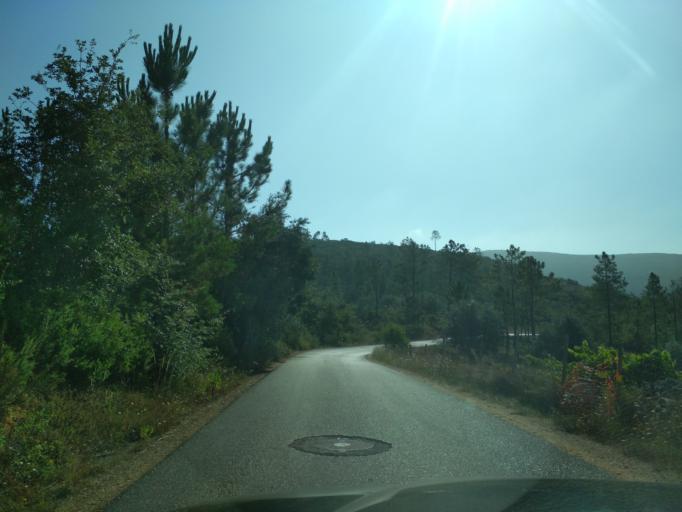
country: PT
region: Coimbra
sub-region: Soure
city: Soure
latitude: 39.9921
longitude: -8.5686
